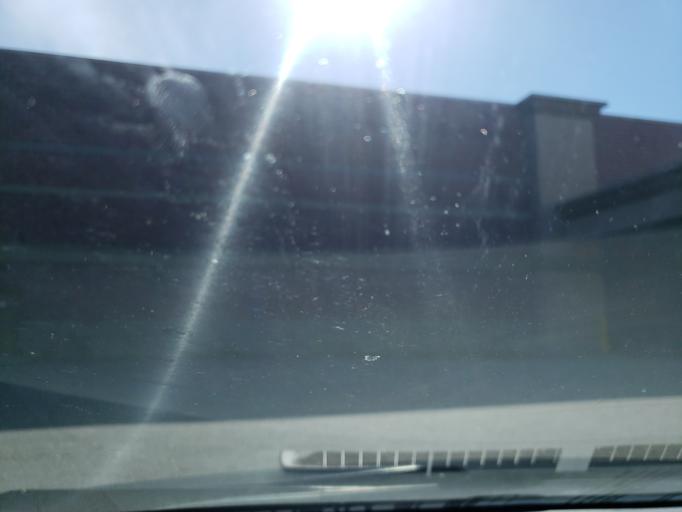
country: US
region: Georgia
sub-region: Chatham County
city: Isle of Hope
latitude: 31.9867
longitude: -81.0804
